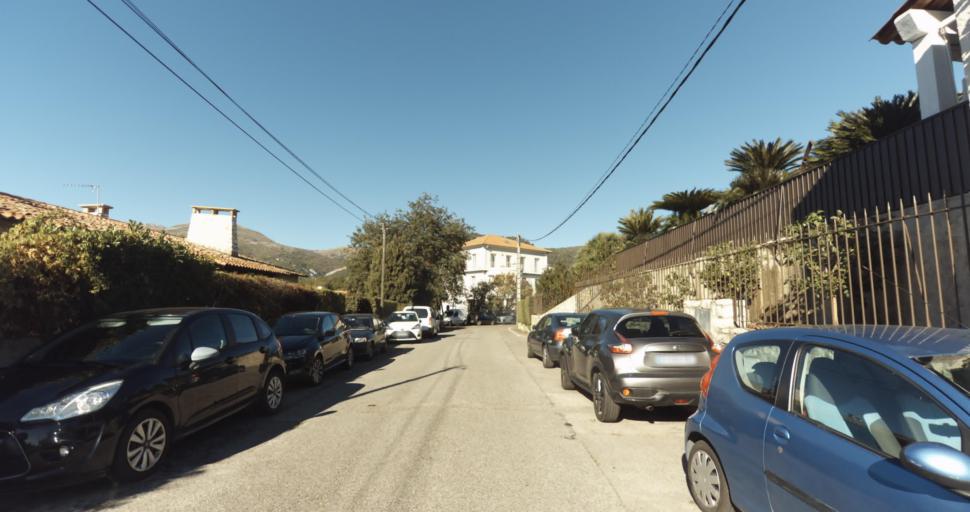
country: FR
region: Provence-Alpes-Cote d'Azur
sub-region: Departement des Alpes-Maritimes
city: Vence
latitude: 43.7192
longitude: 7.1086
